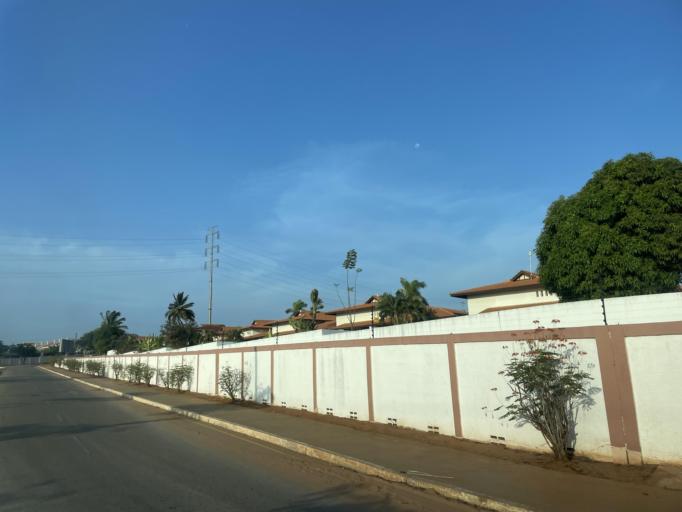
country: AO
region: Luanda
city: Luanda
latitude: -8.9257
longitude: 13.1791
